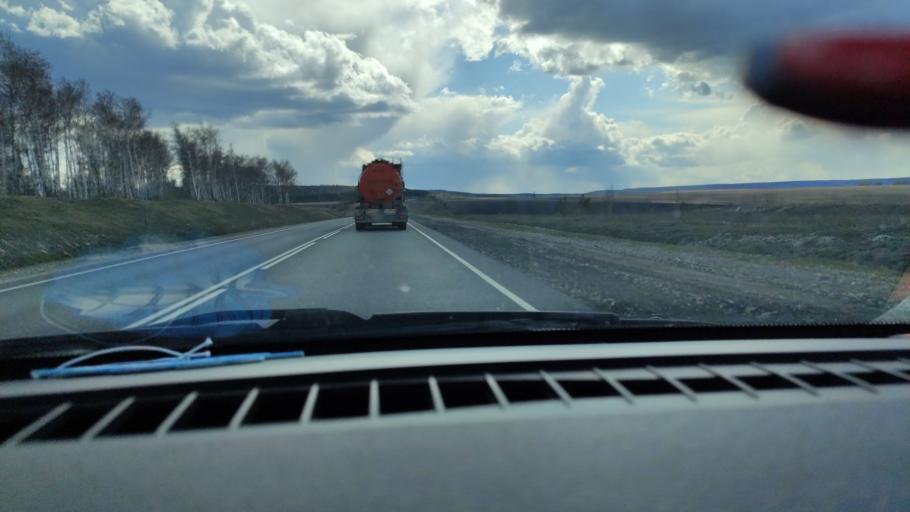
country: RU
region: Saratov
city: Khvalynsk
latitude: 52.5536
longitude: 48.0786
